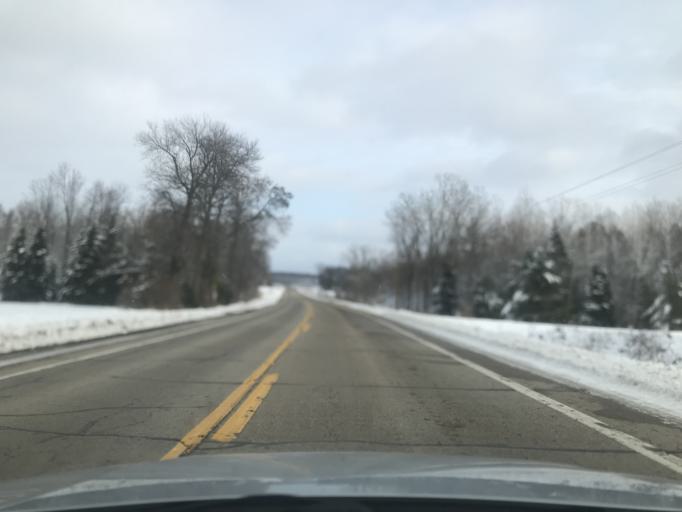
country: US
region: Wisconsin
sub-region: Oconto County
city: Oconto Falls
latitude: 44.8877
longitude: -88.0167
